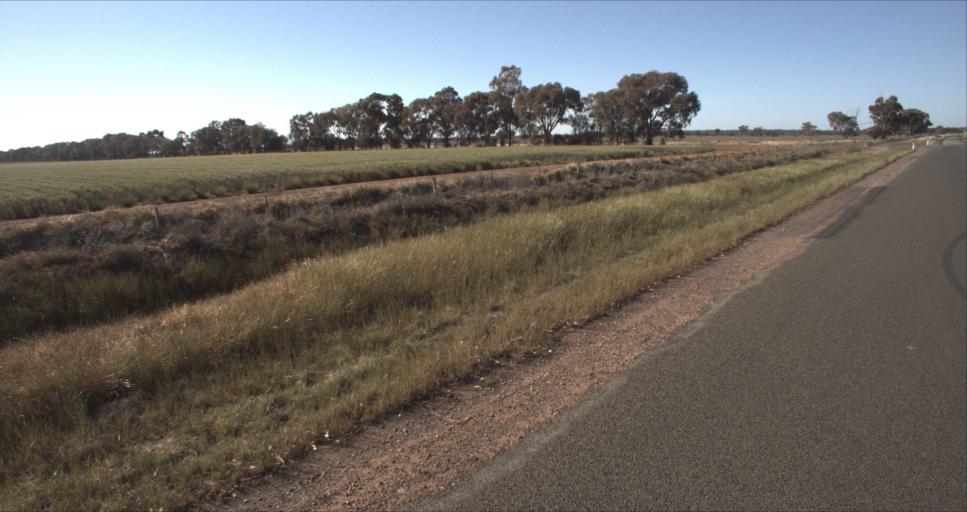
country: AU
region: New South Wales
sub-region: Leeton
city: Leeton
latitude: -34.5765
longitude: 146.2624
